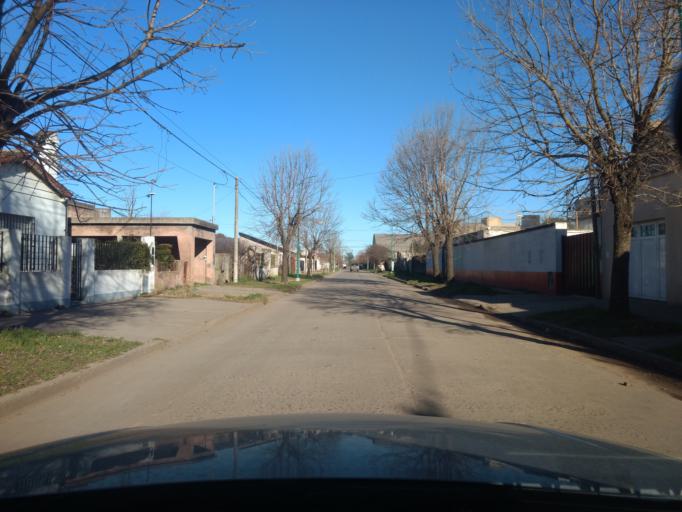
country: AR
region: Buenos Aires
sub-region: Partido de Navarro
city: Navarro
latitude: -35.0006
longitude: -59.2771
